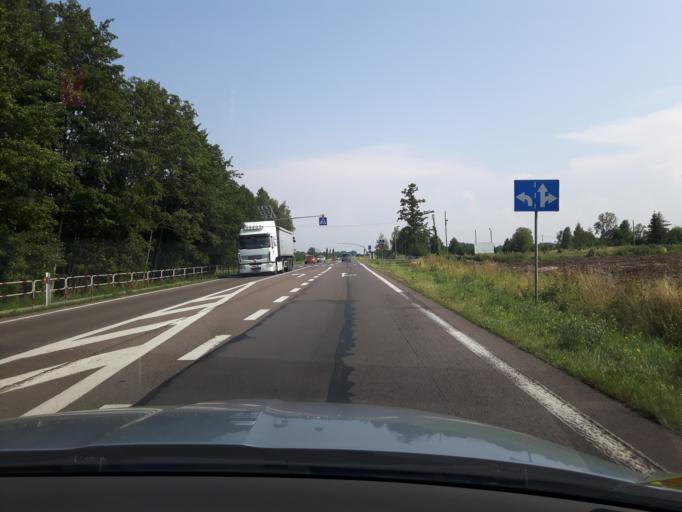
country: PL
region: Masovian Voivodeship
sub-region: Powiat plonski
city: Plonsk
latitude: 52.6963
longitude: 20.3458
